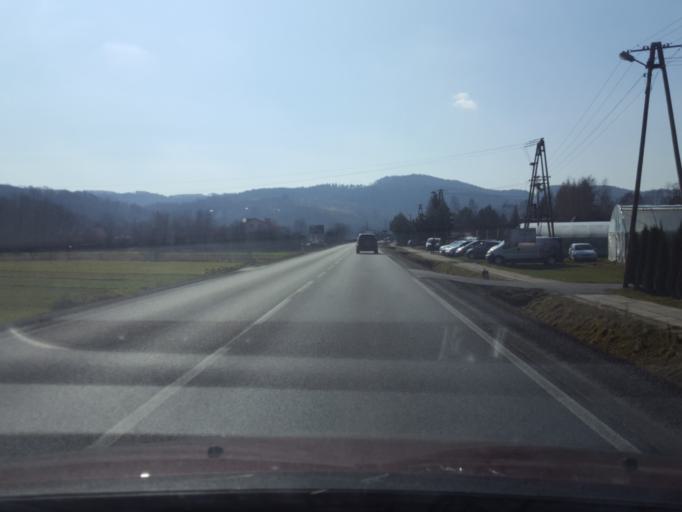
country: PL
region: Lesser Poland Voivodeship
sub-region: Powiat brzeski
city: Czchow
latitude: 49.8270
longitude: 20.6784
